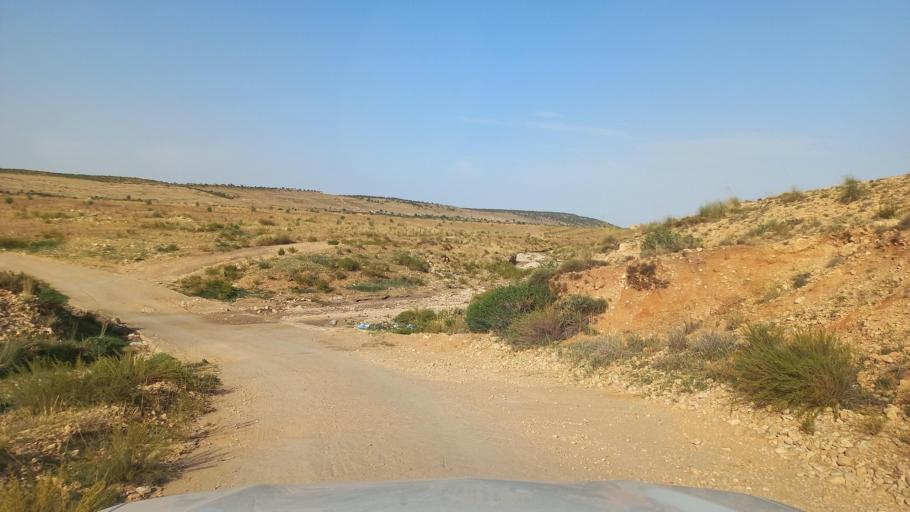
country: TN
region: Al Qasrayn
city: Kasserine
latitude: 35.3568
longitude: 8.8527
